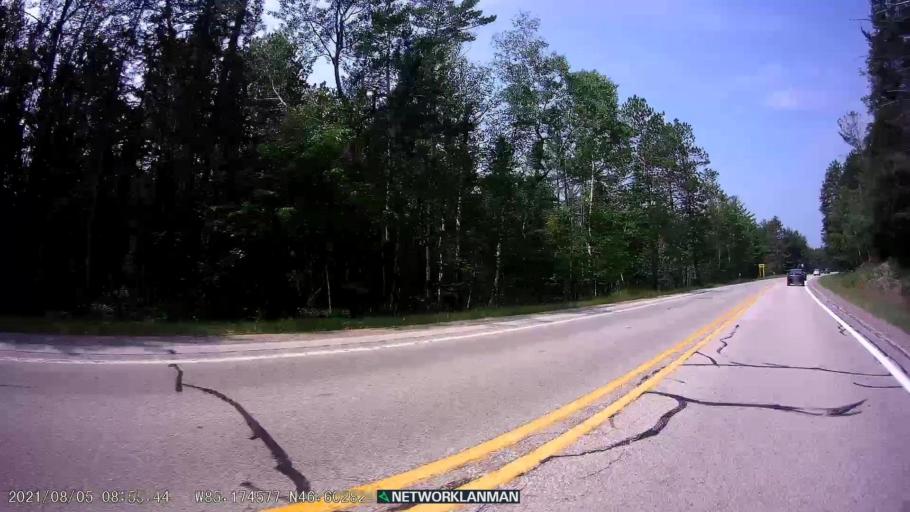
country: US
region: Michigan
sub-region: Luce County
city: Newberry
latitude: 46.6031
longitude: -85.1758
